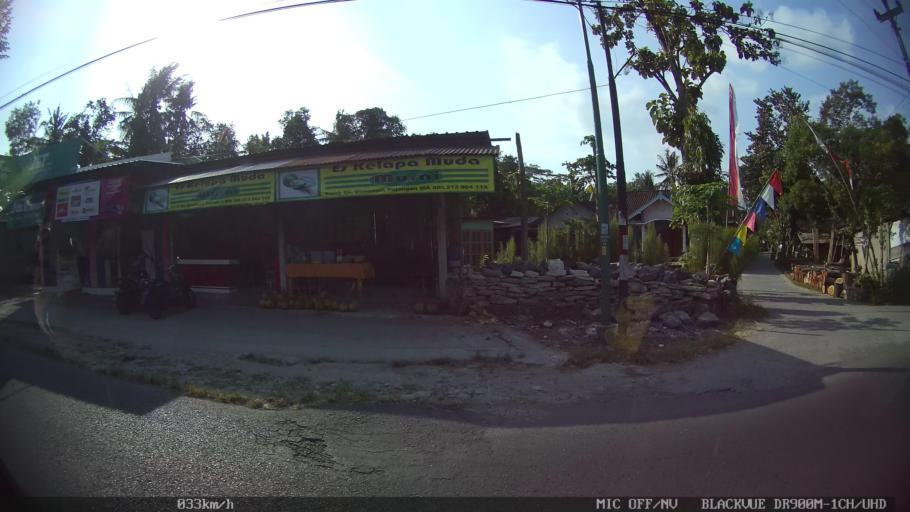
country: ID
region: Daerah Istimewa Yogyakarta
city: Pandak
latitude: -7.8929
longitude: 110.2998
